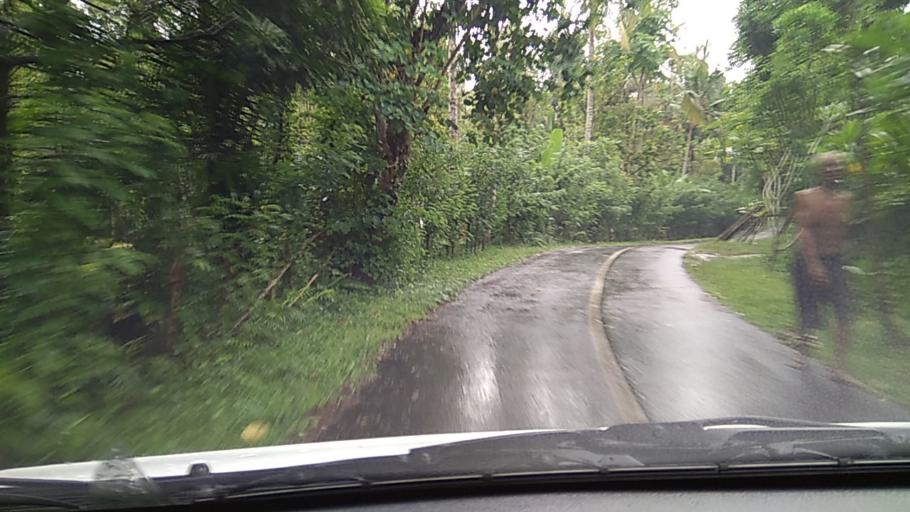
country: ID
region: Bali
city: Tiyingtali Kelod
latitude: -8.4095
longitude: 115.6255
